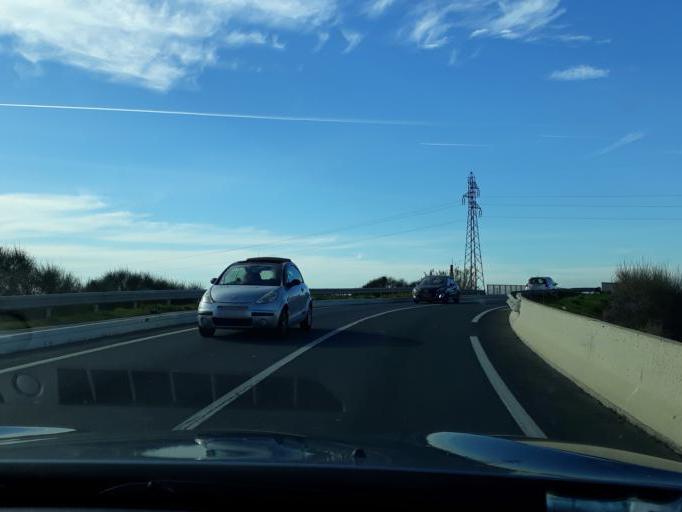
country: FR
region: Languedoc-Roussillon
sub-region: Departement de l'Herault
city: Marseillan
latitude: 43.3199
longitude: 3.5407
